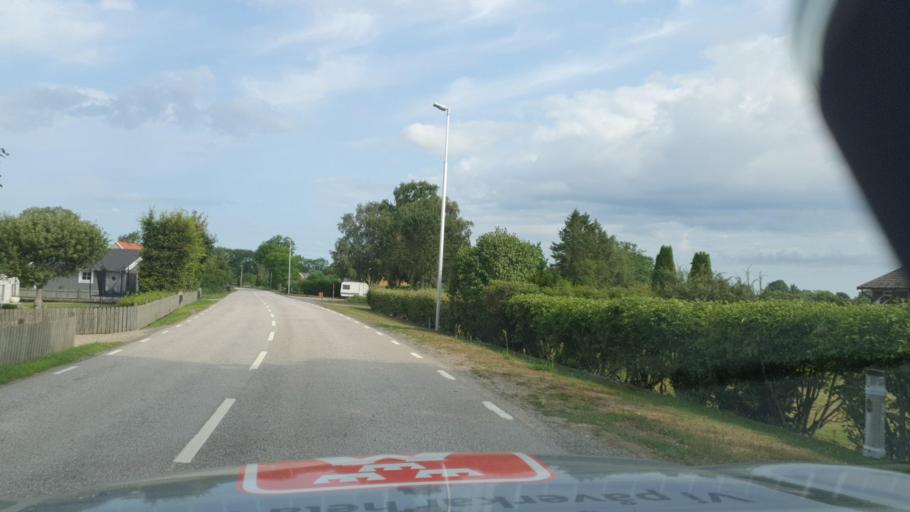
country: SE
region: Blekinge
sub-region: Solvesborgs Kommun
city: Soelvesborg
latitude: 56.0426
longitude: 14.6891
